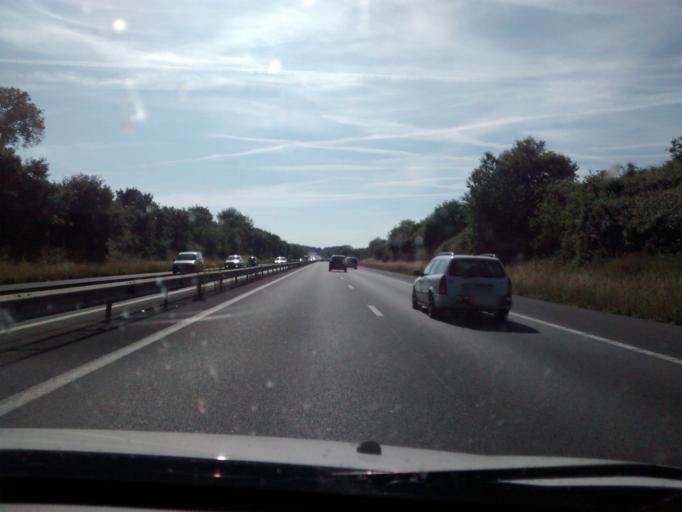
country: FR
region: Brittany
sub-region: Departement d'Ille-et-Vilaine
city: Torce
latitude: 48.0758
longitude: -1.2785
